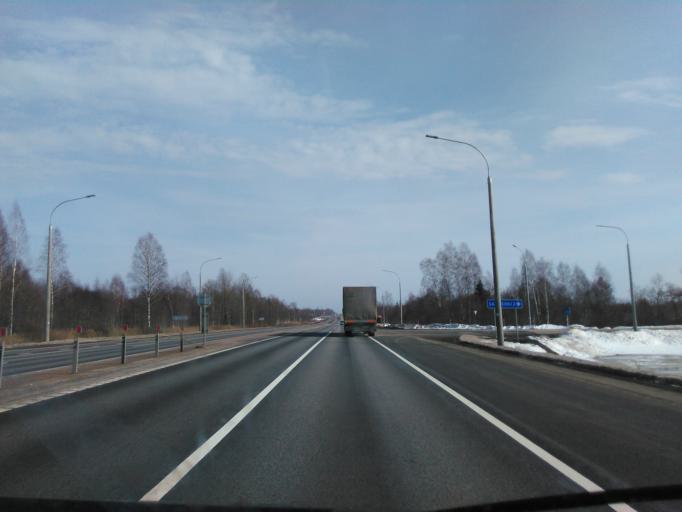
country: BY
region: Vitebsk
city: Dubrowna
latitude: 54.6899
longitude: 30.9307
